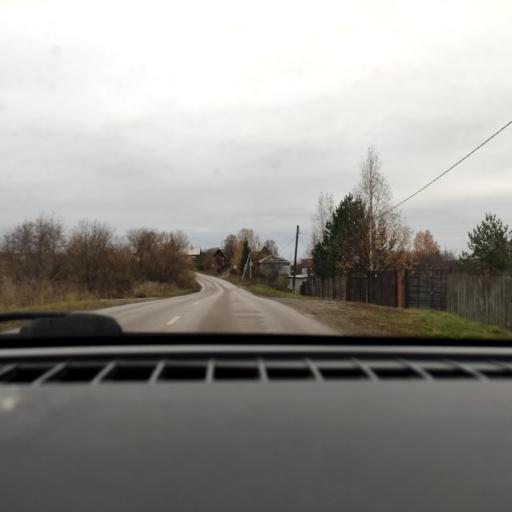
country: RU
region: Perm
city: Ferma
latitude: 57.9237
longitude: 56.3303
